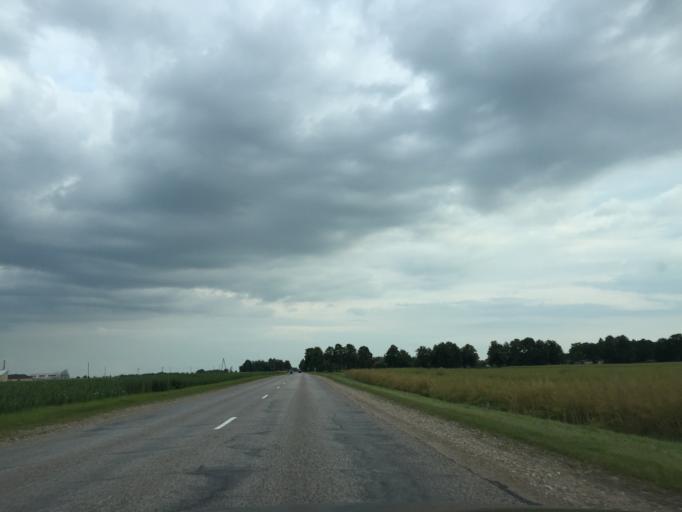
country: LV
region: Dobeles Rajons
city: Dobele
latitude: 56.5732
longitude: 23.2983
